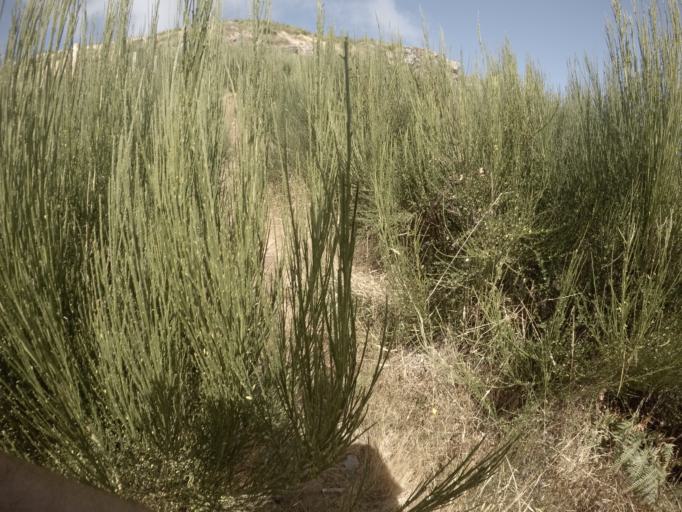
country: PT
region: Madeira
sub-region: Camara de Lobos
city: Curral das Freiras
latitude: 32.7166
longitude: -16.9990
